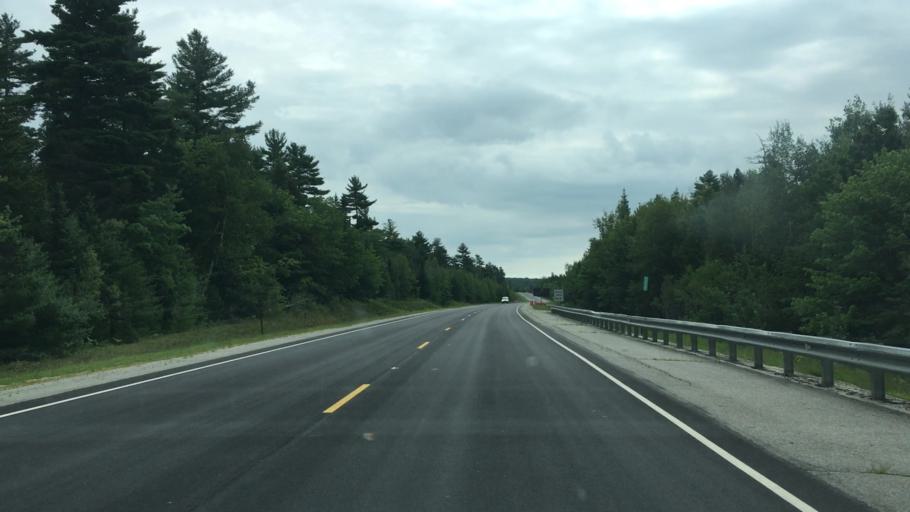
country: US
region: Maine
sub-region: Washington County
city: Addison
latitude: 44.9068
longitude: -67.8284
